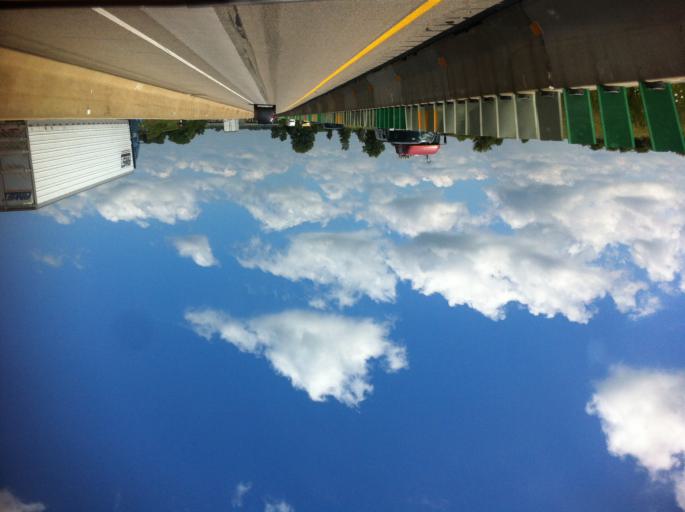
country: US
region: Ohio
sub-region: Huron County
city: Bellevue
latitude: 41.3529
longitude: -82.8690
